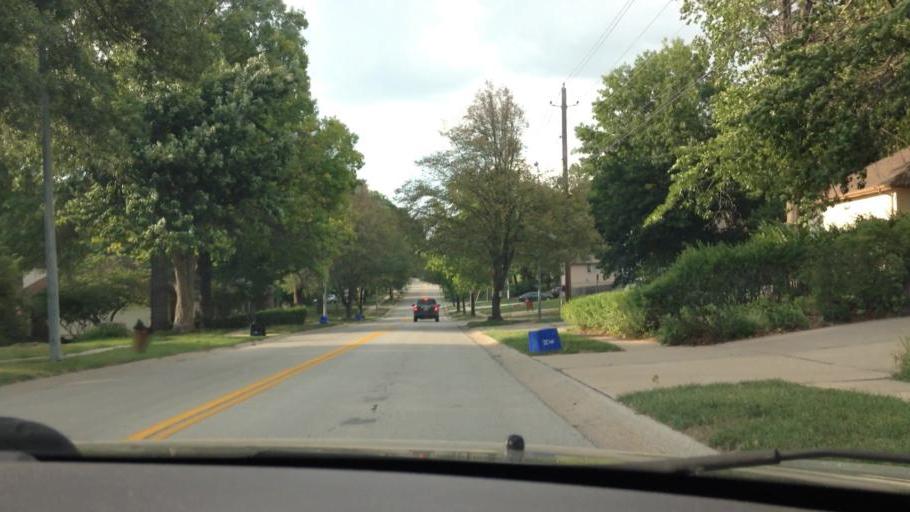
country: US
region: Missouri
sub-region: Platte County
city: Parkville
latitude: 39.2164
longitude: -94.6405
